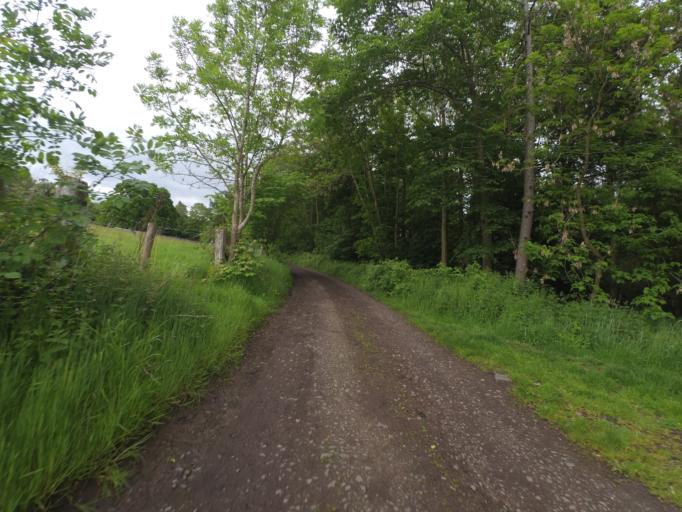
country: GB
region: Scotland
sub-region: East Lothian
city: Musselburgh
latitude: 55.9122
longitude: -3.0172
